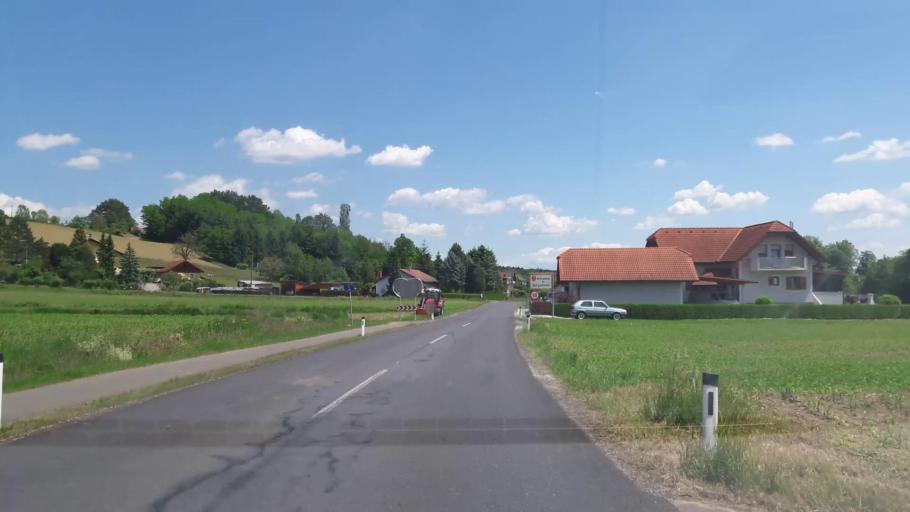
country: AT
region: Styria
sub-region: Politischer Bezirk Hartberg-Fuerstenfeld
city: Loipersdorf bei Fuerstenfeld
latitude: 46.9628
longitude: 16.1033
